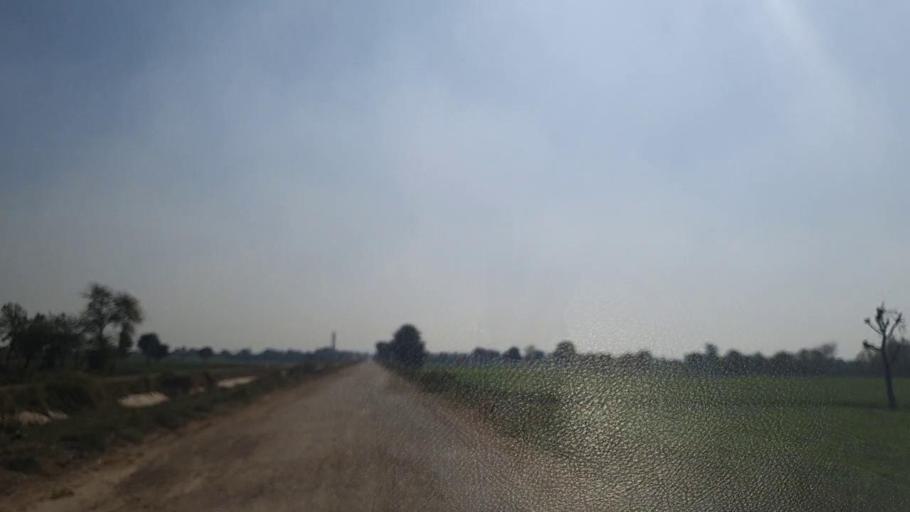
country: PK
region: Sindh
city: Shahpur Chakar
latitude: 26.1944
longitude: 68.5836
